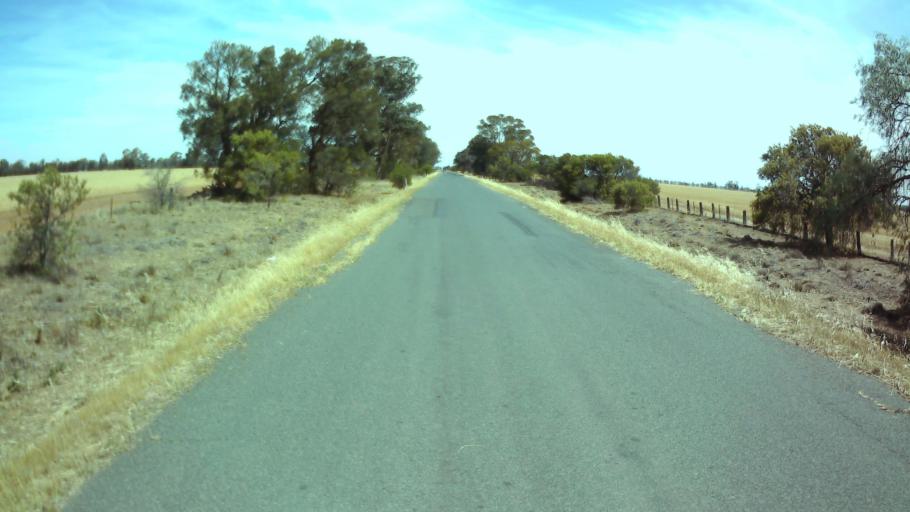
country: AU
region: New South Wales
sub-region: Weddin
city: Grenfell
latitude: -33.9503
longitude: 147.7778
